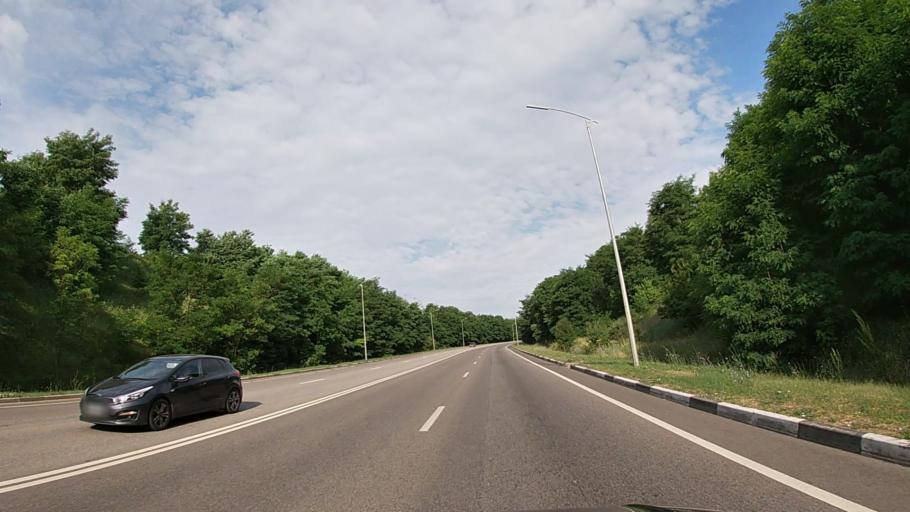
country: RU
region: Belgorod
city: Severnyy
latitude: 50.6358
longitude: 36.4547
